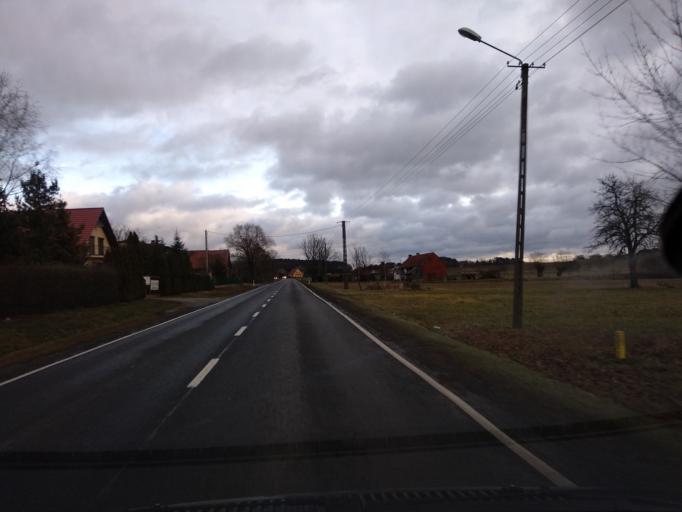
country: PL
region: Lower Silesian Voivodeship
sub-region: Powiat olesnicki
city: Miedzyborz
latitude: 51.3729
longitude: 17.6217
